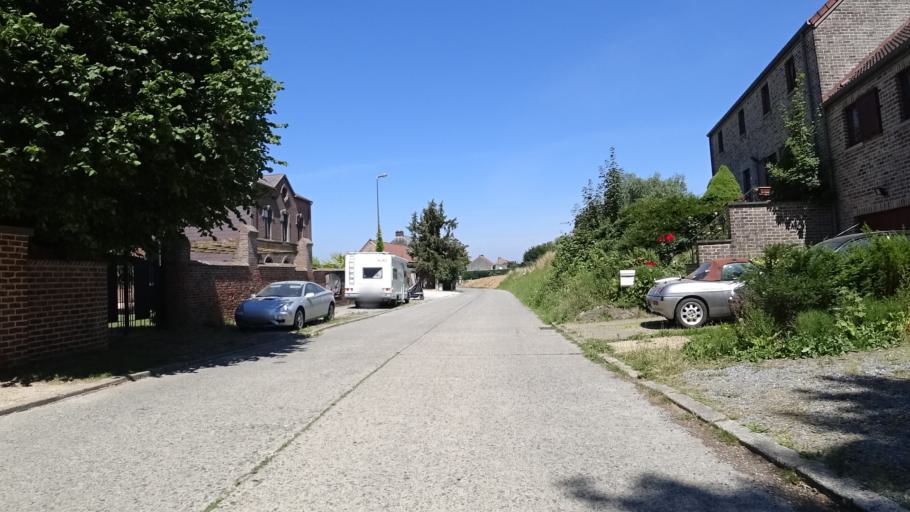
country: BE
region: Wallonia
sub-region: Province du Brabant Wallon
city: Incourt
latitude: 50.6775
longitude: 4.8344
